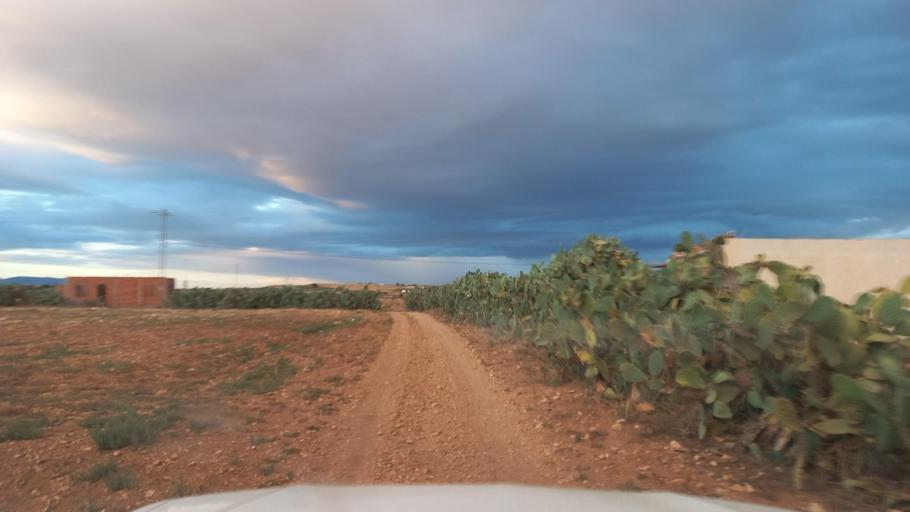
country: TN
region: Al Qasrayn
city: Kasserine
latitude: 35.2622
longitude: 8.9385
